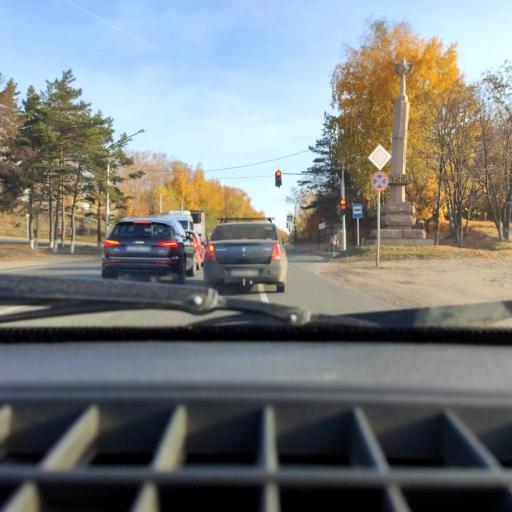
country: RU
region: Bashkortostan
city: Avdon
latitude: 54.6808
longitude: 55.8074
